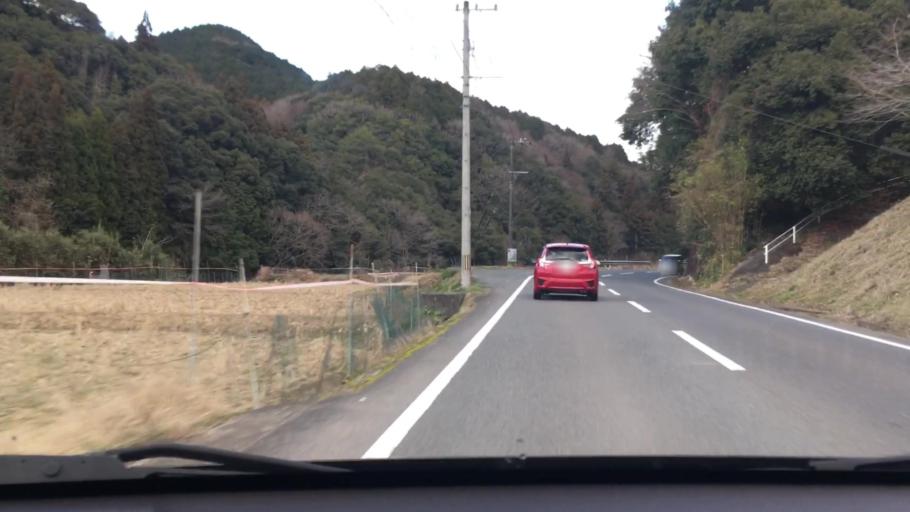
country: JP
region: Oita
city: Bungo-Takada-shi
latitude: 33.4519
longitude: 131.3926
